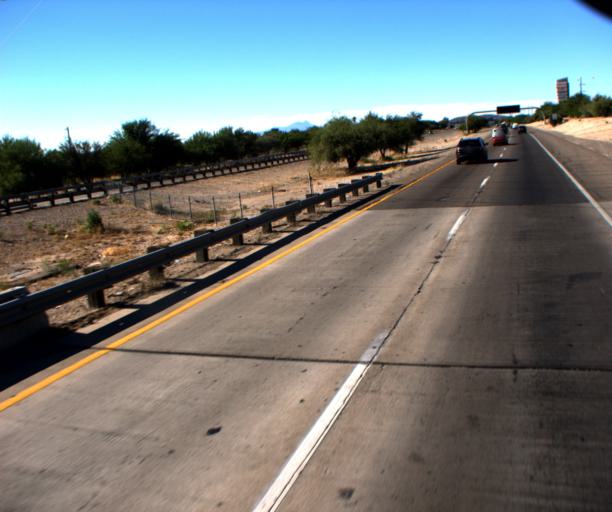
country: US
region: Arizona
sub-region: Pima County
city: Drexel Heights
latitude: 32.1553
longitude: -110.9865
